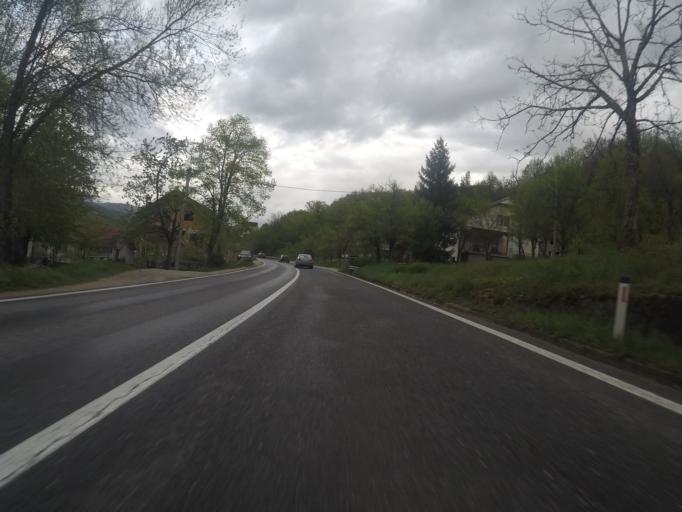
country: BA
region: Federation of Bosnia and Herzegovina
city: Konjic
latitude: 43.6754
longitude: 17.9080
